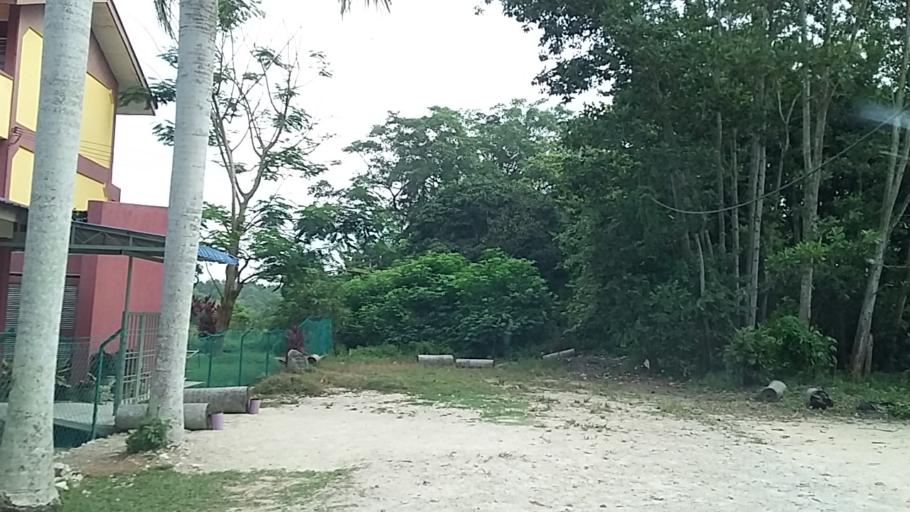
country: MY
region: Johor
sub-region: Daerah Batu Pahat
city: Batu Pahat
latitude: 1.7920
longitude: 102.8935
